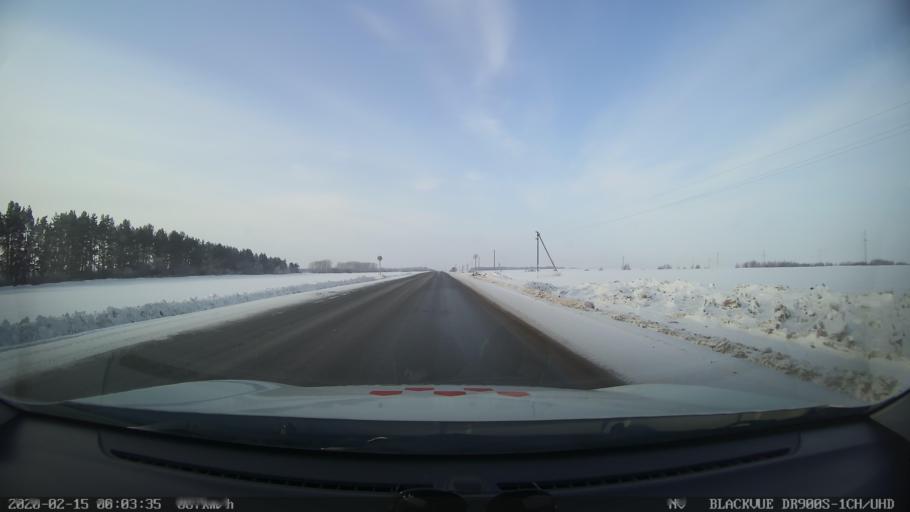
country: RU
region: Tatarstan
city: Kuybyshevskiy Zaton
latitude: 55.3734
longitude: 48.9959
